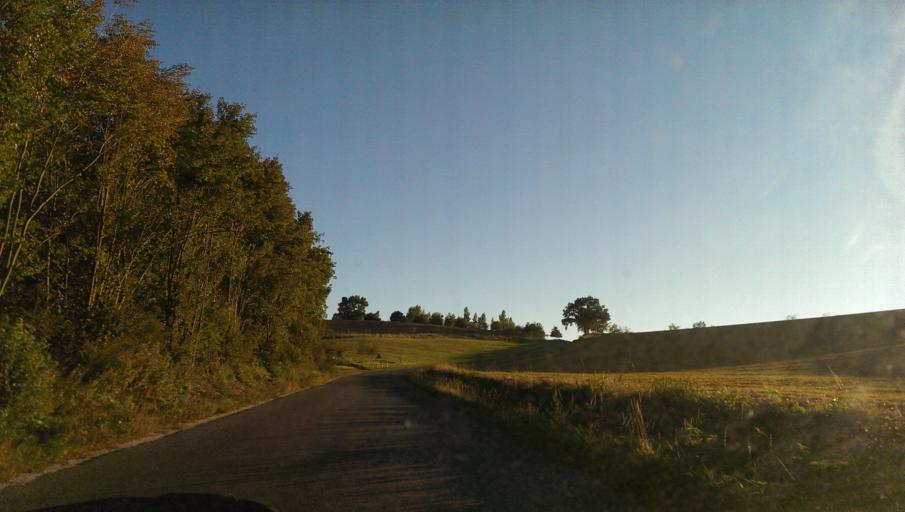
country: CZ
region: Zlin
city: Velehrad
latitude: 49.0994
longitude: 17.3887
